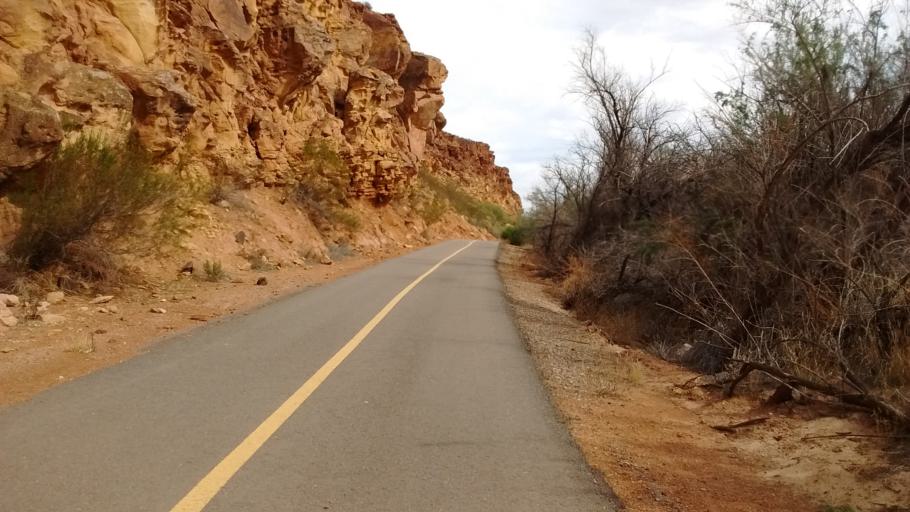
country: US
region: Utah
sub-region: Washington County
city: Washington
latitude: 37.1219
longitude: -113.4818
